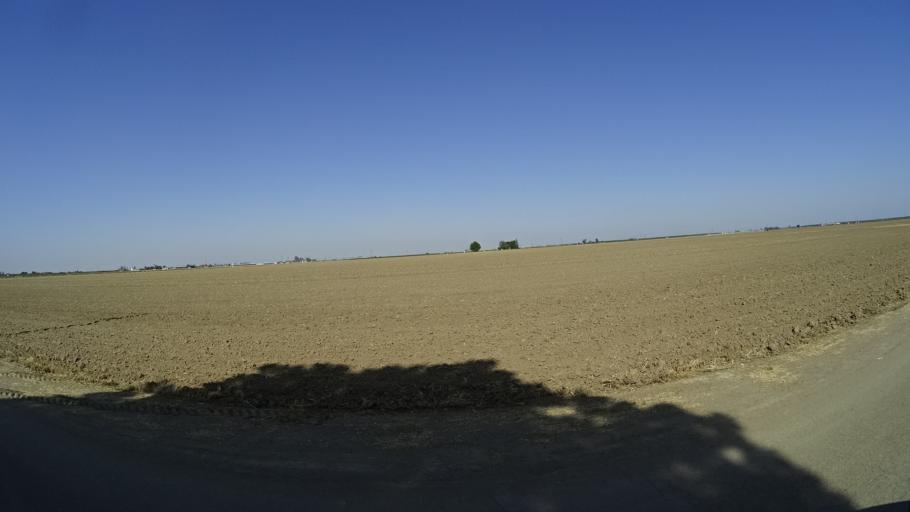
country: US
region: California
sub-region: Kings County
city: Home Garden
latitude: 36.2351
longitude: -119.5742
